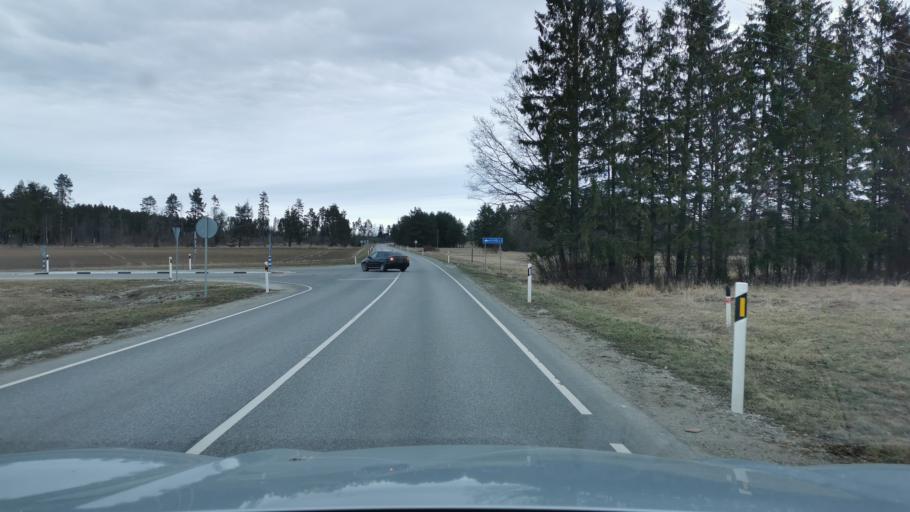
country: EE
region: Ida-Virumaa
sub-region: Puessi linn
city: Pussi
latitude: 59.3569
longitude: 27.0232
